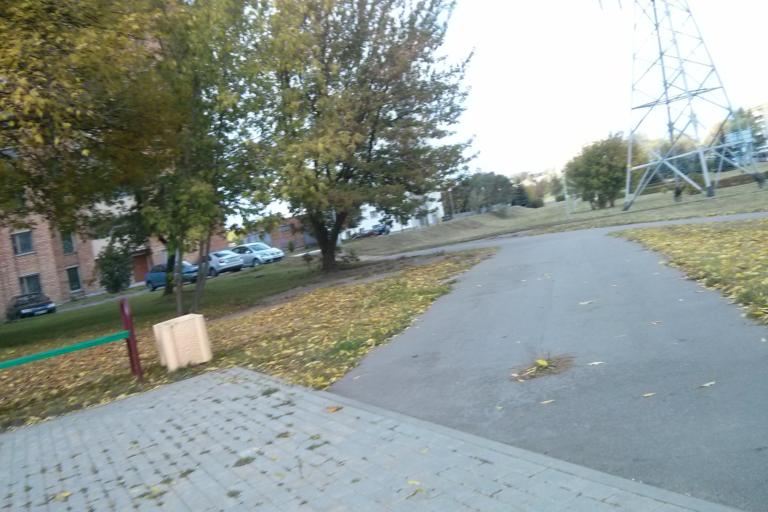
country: BY
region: Minsk
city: Minsk
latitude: 53.8787
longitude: 27.5979
